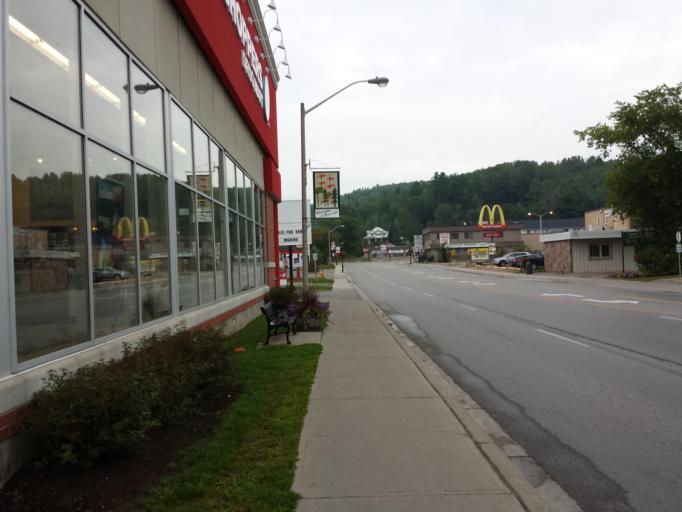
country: CA
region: Ontario
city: Bancroft
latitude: 45.0615
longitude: -77.8563
